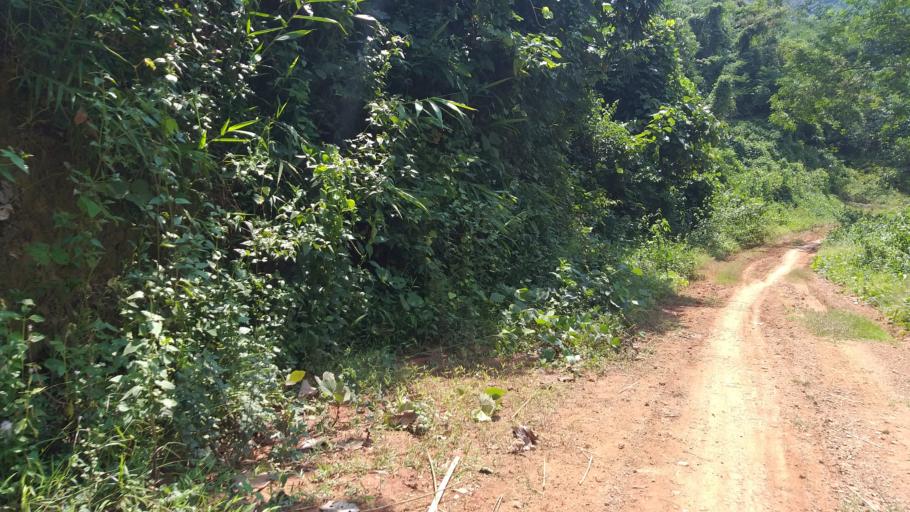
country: LA
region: Phongsali
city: Khoa
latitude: 21.3047
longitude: 102.5579
